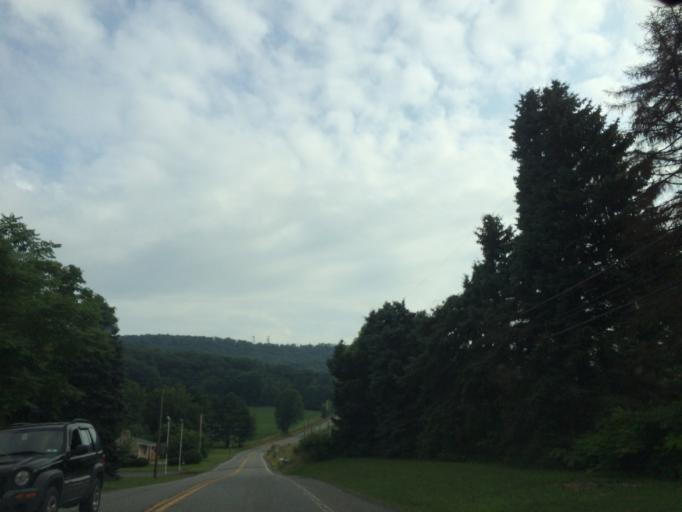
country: US
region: Pennsylvania
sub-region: Dauphin County
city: Matamoras
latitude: 40.4210
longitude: -76.9425
